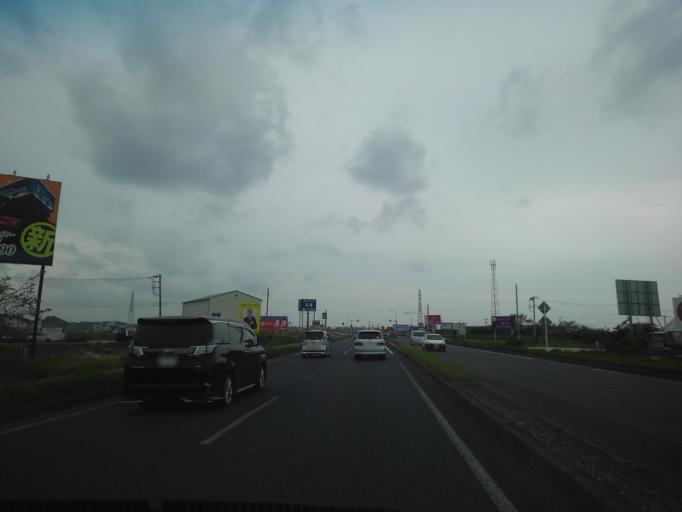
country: JP
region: Chiba
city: Kisarazu
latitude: 35.4059
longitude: 139.9444
